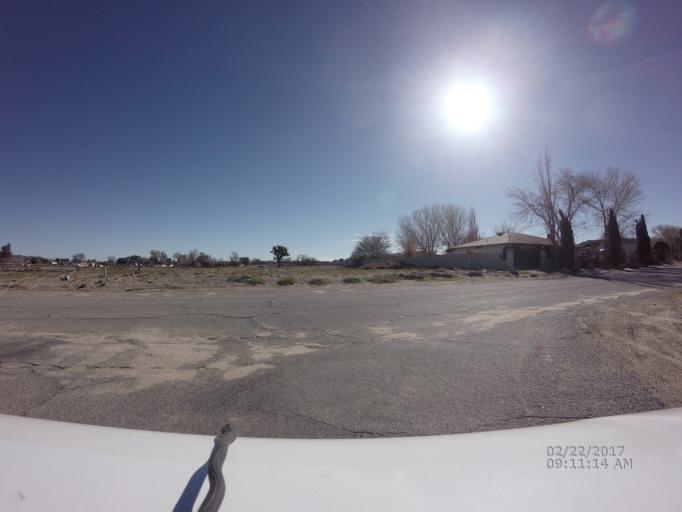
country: US
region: California
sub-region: Los Angeles County
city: Lake Los Angeles
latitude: 34.6210
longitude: -117.8554
